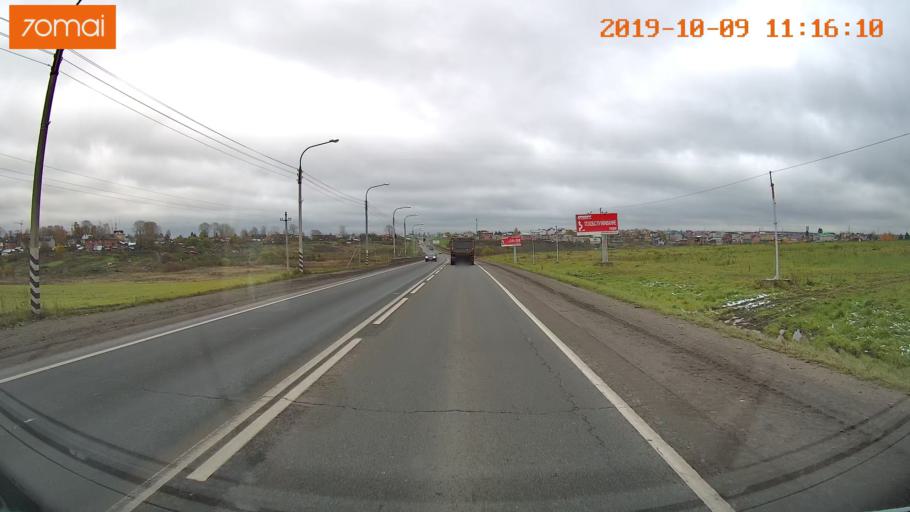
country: RU
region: Vologda
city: Vologda
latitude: 59.1785
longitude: 39.8800
